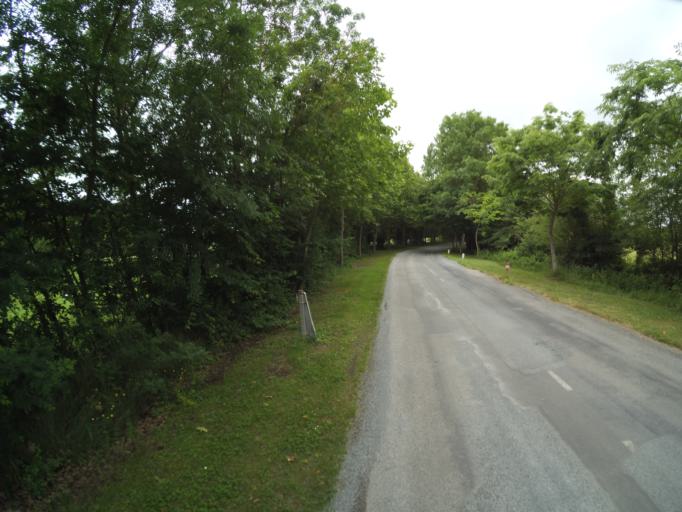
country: FR
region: Poitou-Charentes
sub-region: Departement de la Charente-Maritime
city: Saint-Laurent-de-la-Pree
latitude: 45.9826
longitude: -1.0043
